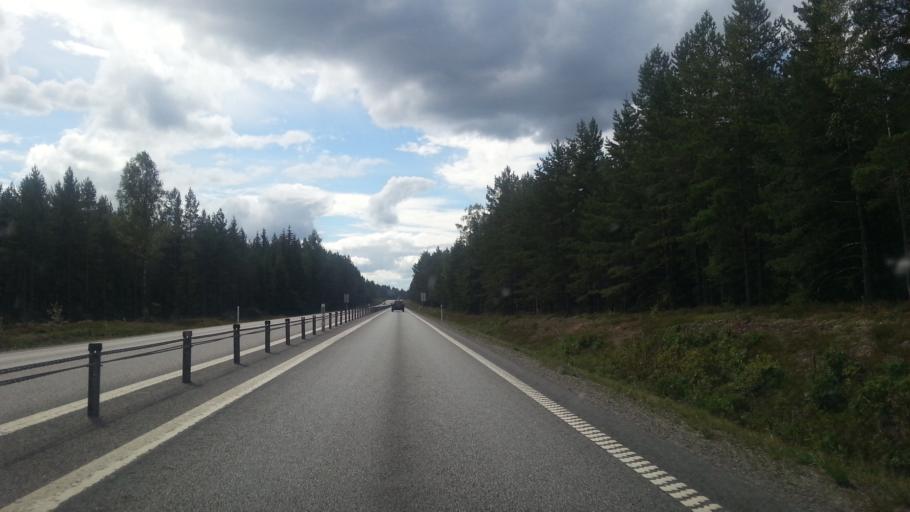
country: SE
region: OErebro
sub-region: Lindesbergs Kommun
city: Lindesberg
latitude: 59.5397
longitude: 15.2041
